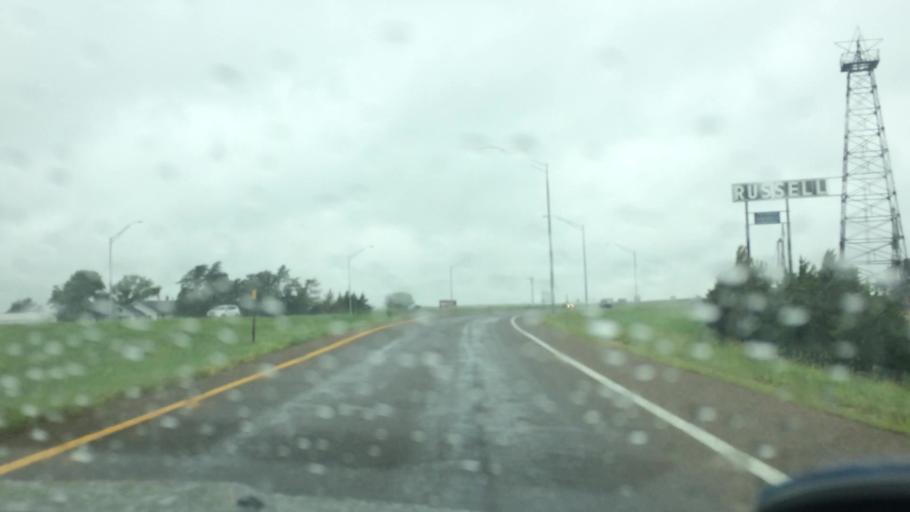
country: US
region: Kansas
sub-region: Russell County
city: Russell
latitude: 38.8647
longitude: -98.8568
